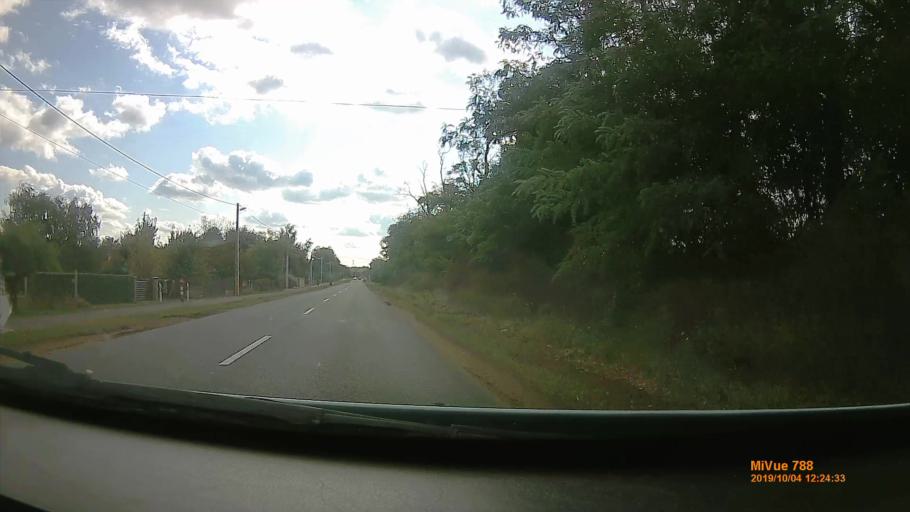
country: HU
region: Szabolcs-Szatmar-Bereg
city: Nyiregyhaza
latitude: 47.9951
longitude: 21.7029
